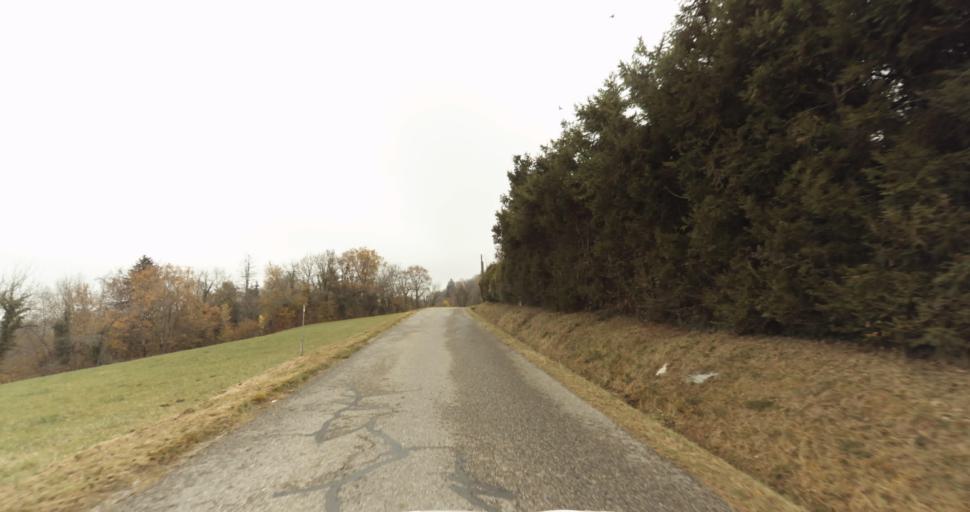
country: FR
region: Rhone-Alpes
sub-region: Departement de la Haute-Savoie
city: Viuz-la-Chiesaz
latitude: 45.8291
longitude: 6.0739
